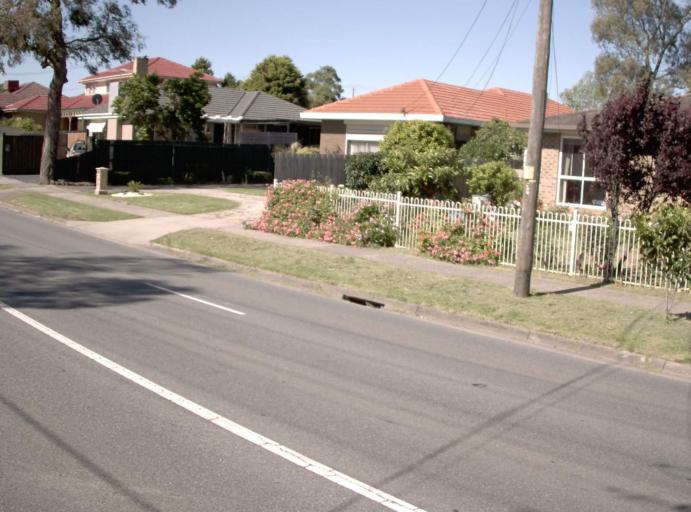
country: AU
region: Victoria
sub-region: Knox
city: Knoxfield
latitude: -37.8725
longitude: 145.2596
